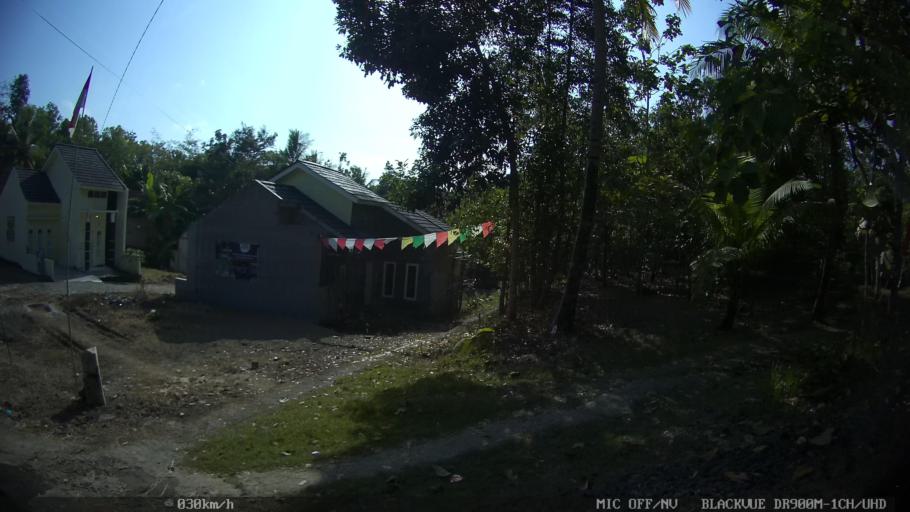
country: ID
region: Daerah Istimewa Yogyakarta
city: Kasihan
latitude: -7.8288
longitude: 110.2735
